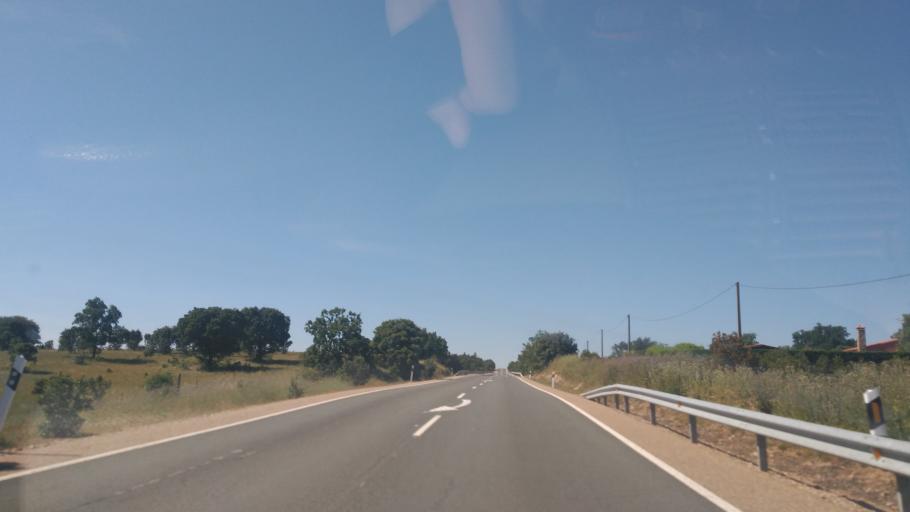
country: ES
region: Castille and Leon
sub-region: Provincia de Zamora
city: Cuelgamures
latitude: 41.2720
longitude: -5.7159
